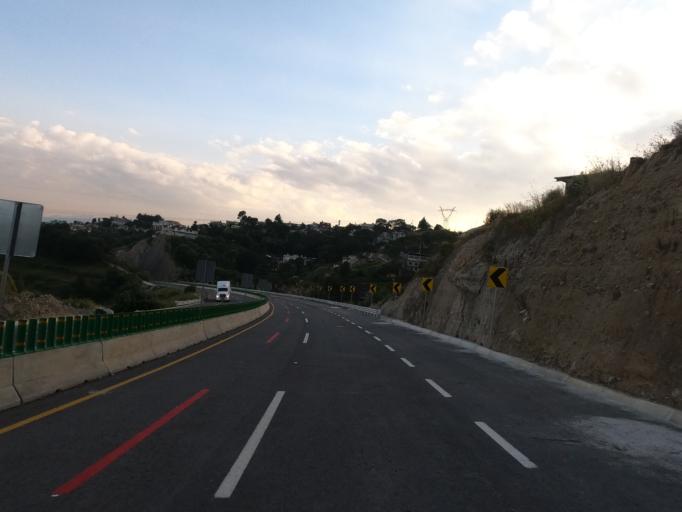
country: MX
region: Mexico
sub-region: Naucalpan de Juarez
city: Llano de las Flores (Barrio del Hueso)
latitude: 19.4278
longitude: -99.3326
